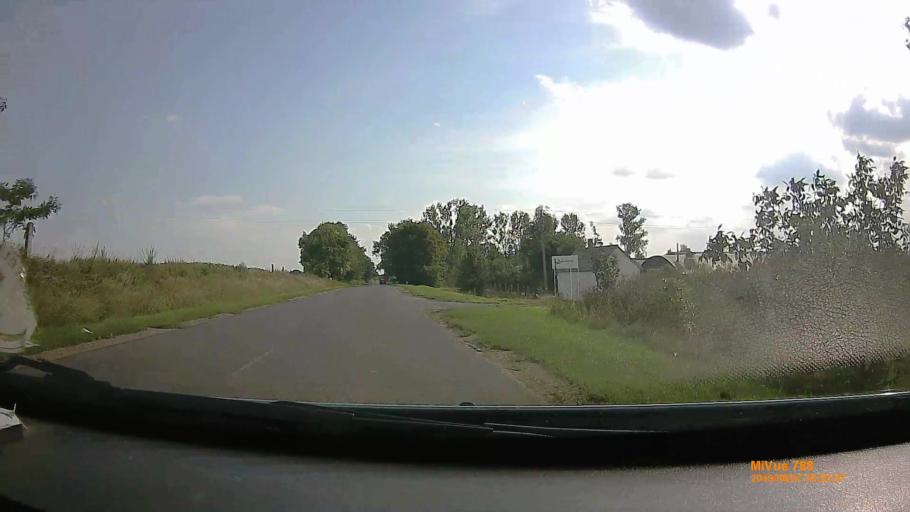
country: HU
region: Borsod-Abauj-Zemplen
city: Gonc
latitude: 48.3956
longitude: 21.2237
